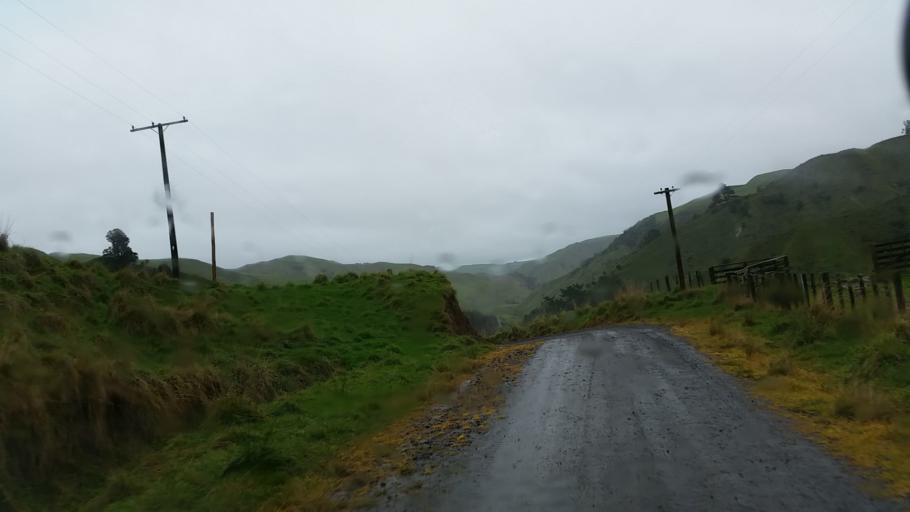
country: NZ
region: Taranaki
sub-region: South Taranaki District
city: Eltham
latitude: -39.4762
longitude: 174.4111
